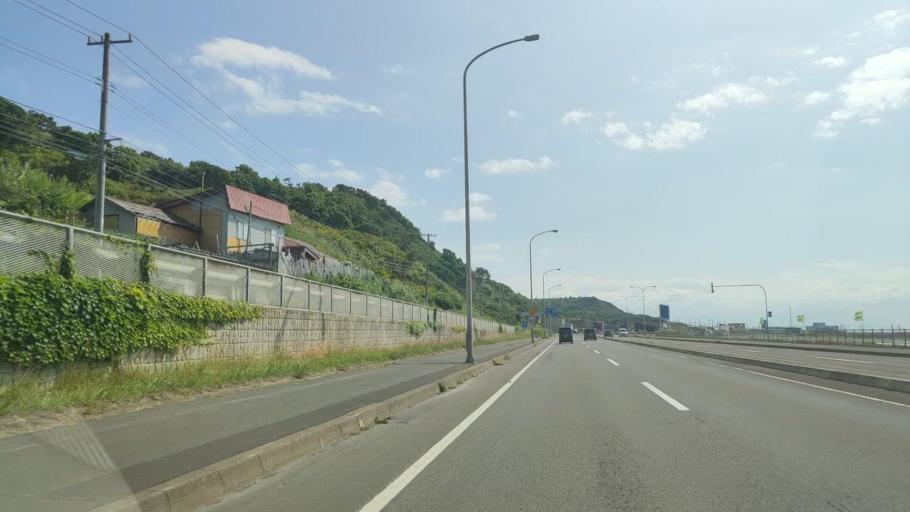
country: JP
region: Hokkaido
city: Rumoi
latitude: 44.0027
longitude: 141.6583
